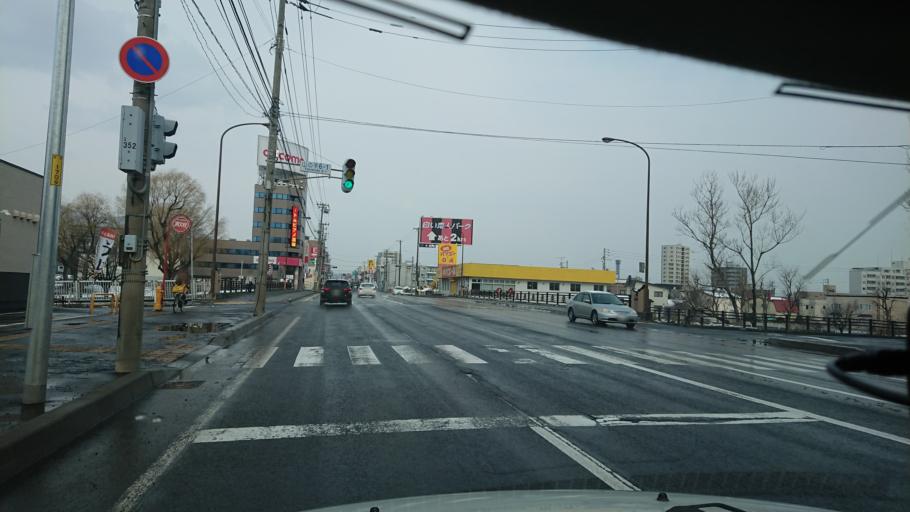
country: JP
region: Hokkaido
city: Sapporo
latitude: 43.0763
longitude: 141.2941
